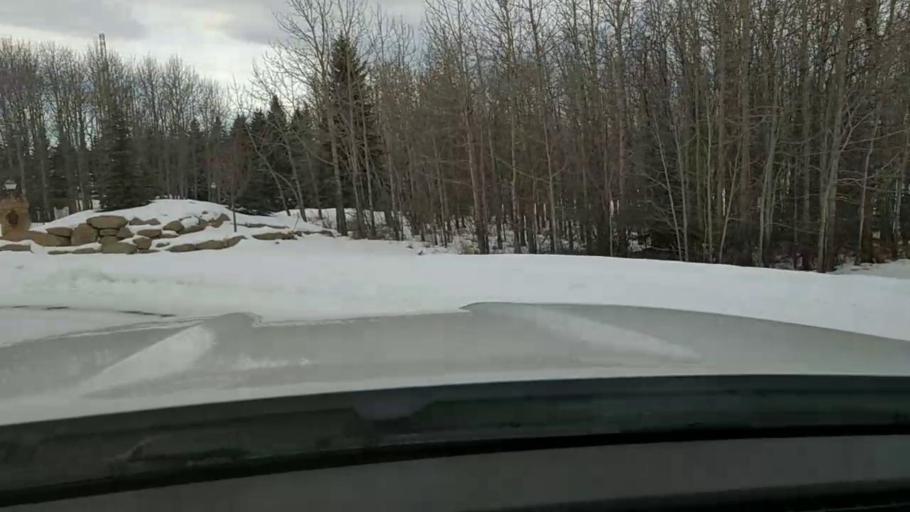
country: CA
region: Alberta
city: Cochrane
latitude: 51.1862
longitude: -114.2542
